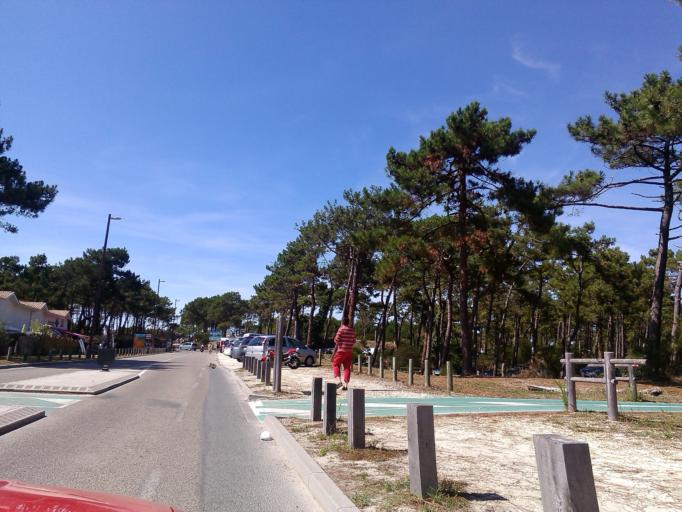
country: FR
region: Aquitaine
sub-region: Departement de la Gironde
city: Lacanau
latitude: 45.0074
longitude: -1.1942
